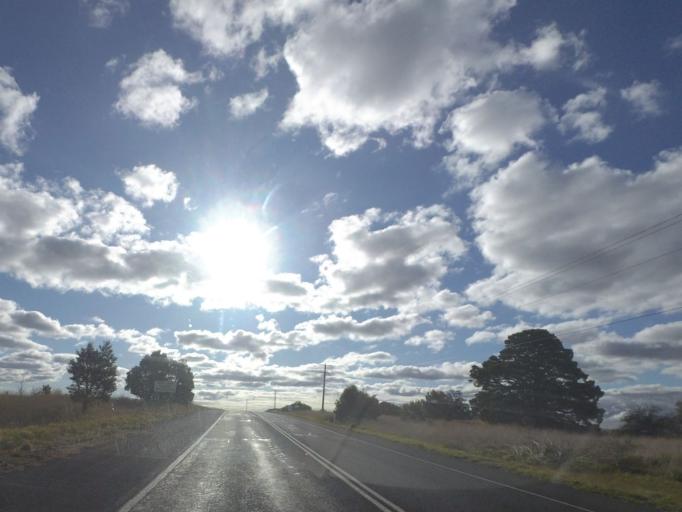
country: AU
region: Victoria
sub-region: Mount Alexander
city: Castlemaine
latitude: -37.1800
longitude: 144.3613
